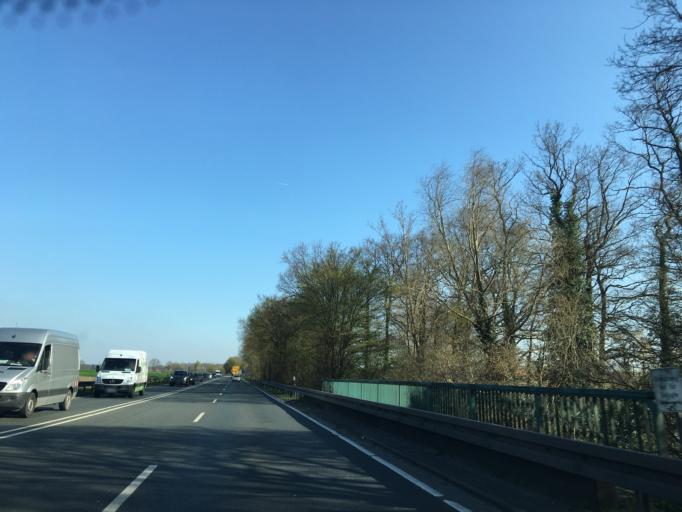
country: DE
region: North Rhine-Westphalia
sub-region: Regierungsbezirk Munster
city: Greven
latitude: 52.0901
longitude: 7.6355
